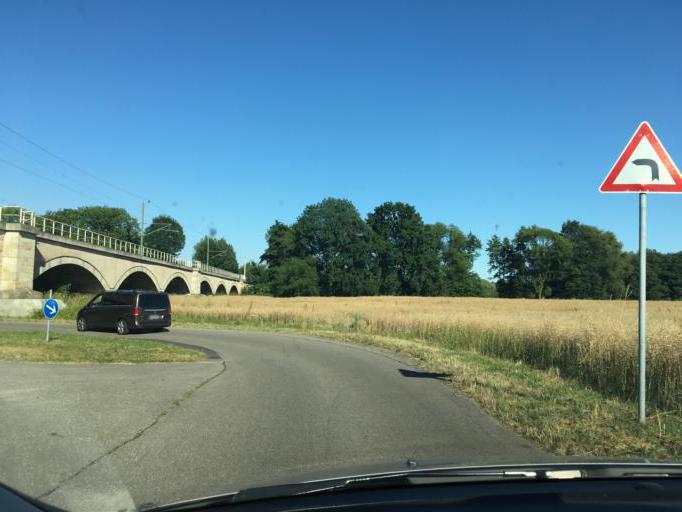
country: DE
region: Saxony
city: Borna
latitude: 51.0960
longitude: 12.5115
